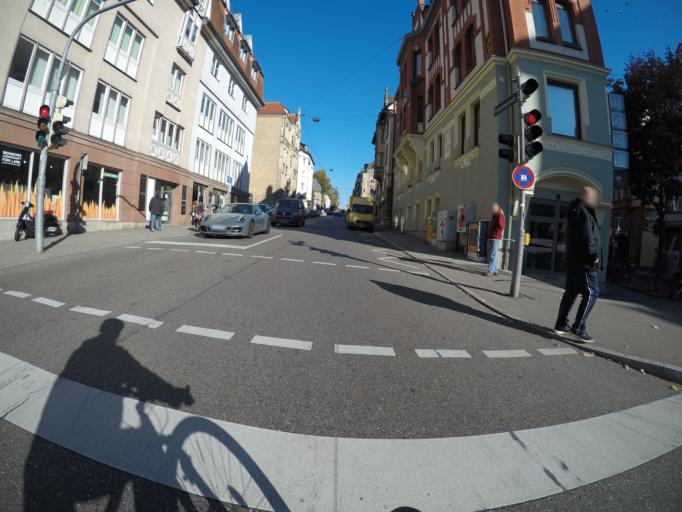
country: DE
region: Baden-Wuerttemberg
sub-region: Regierungsbezirk Stuttgart
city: Stuttgart
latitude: 48.7649
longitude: 9.1681
